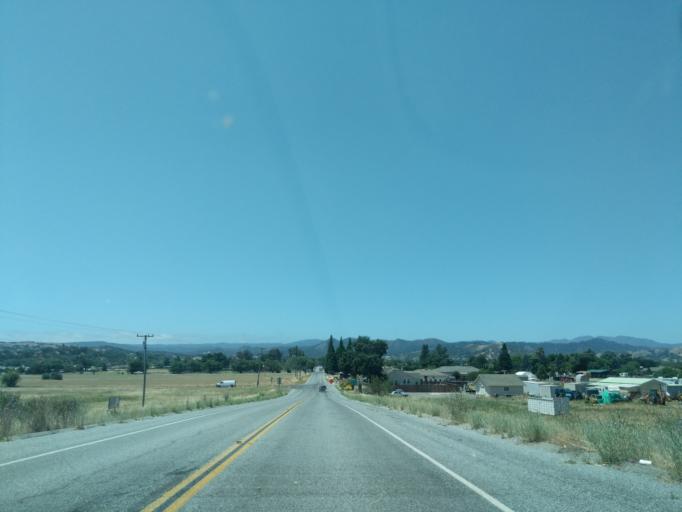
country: US
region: California
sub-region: Santa Clara County
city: San Martin
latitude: 37.1041
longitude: -121.6122
